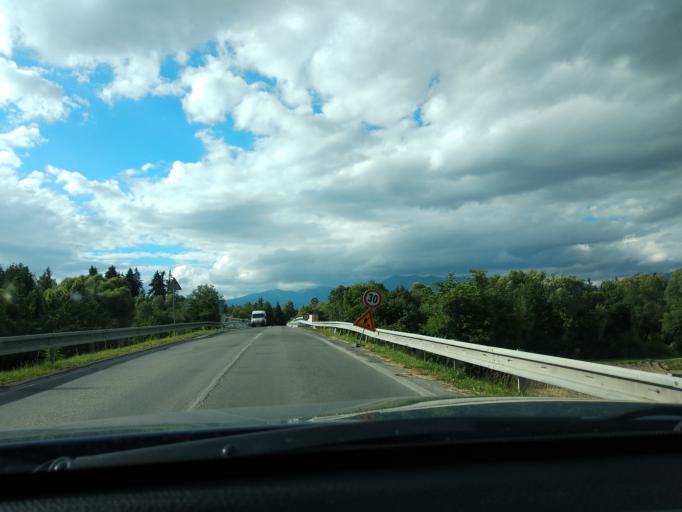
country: SK
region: Zilinsky
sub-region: Okres Zilina
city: Liptovsky Hradok
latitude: 49.0455
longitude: 19.7313
